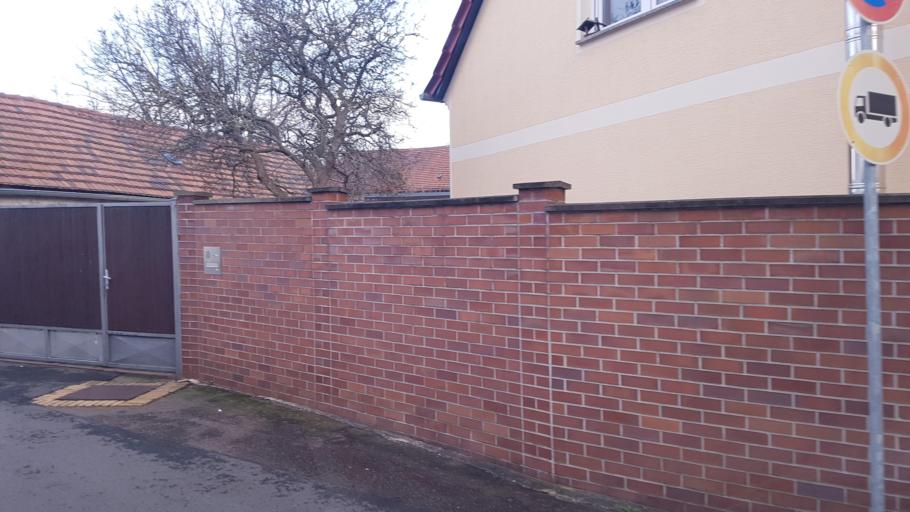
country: DE
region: Brandenburg
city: Lauchhammer
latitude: 51.4962
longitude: 13.7589
